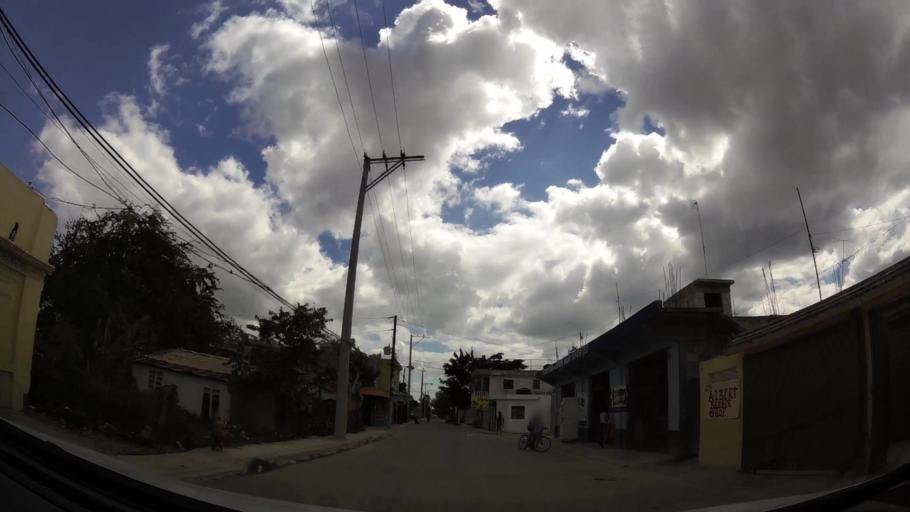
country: DO
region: Santo Domingo
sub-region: Santo Domingo
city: Boca Chica
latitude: 18.4531
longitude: -69.6446
